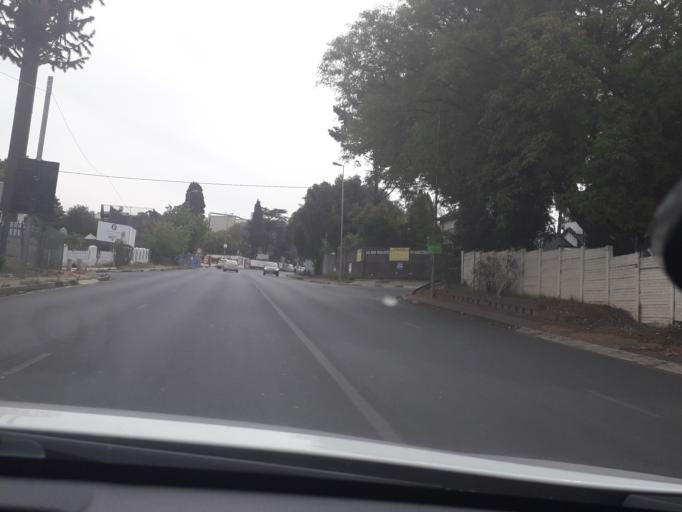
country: ZA
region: Gauteng
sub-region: City of Johannesburg Metropolitan Municipality
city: Johannesburg
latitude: -26.1004
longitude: 28.0063
